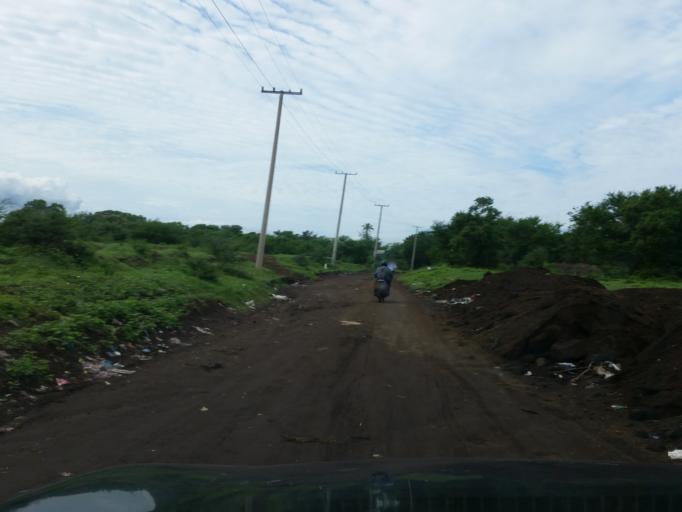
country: NI
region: Managua
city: Managua
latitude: 12.0989
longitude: -86.2064
